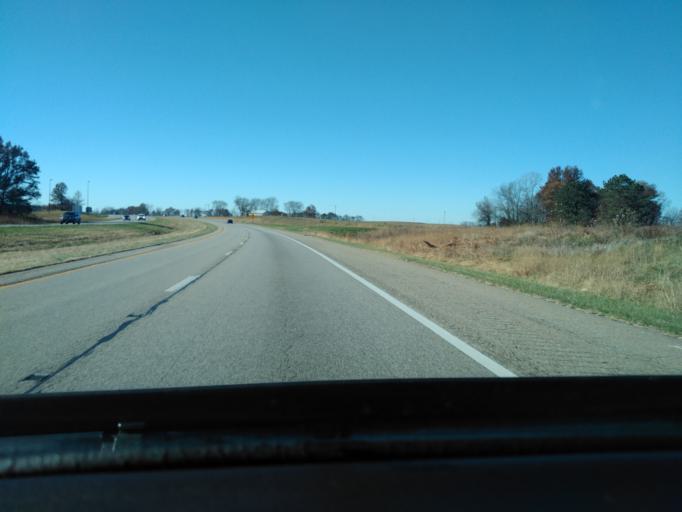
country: US
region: Illinois
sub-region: Bond County
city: Greenville
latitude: 38.8316
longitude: -89.5463
